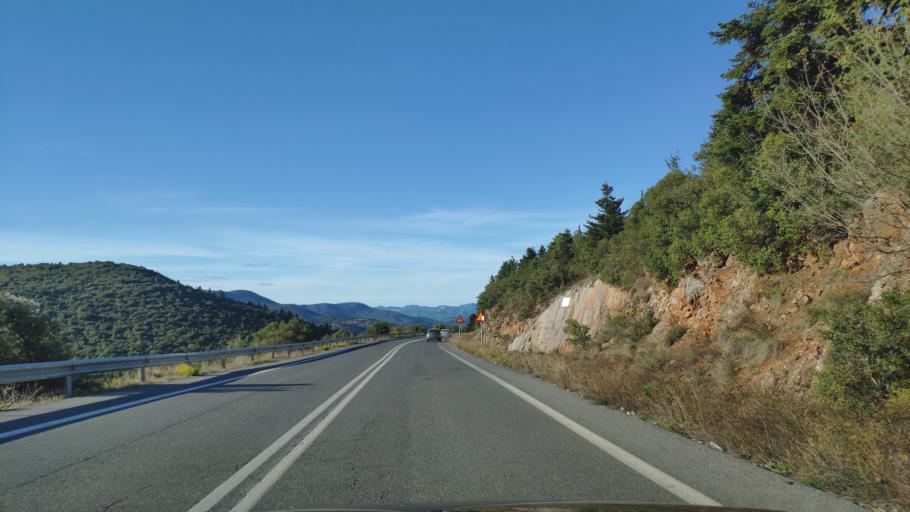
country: GR
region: Peloponnese
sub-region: Nomos Arkadias
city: Langadhia
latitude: 37.6997
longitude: 22.1984
